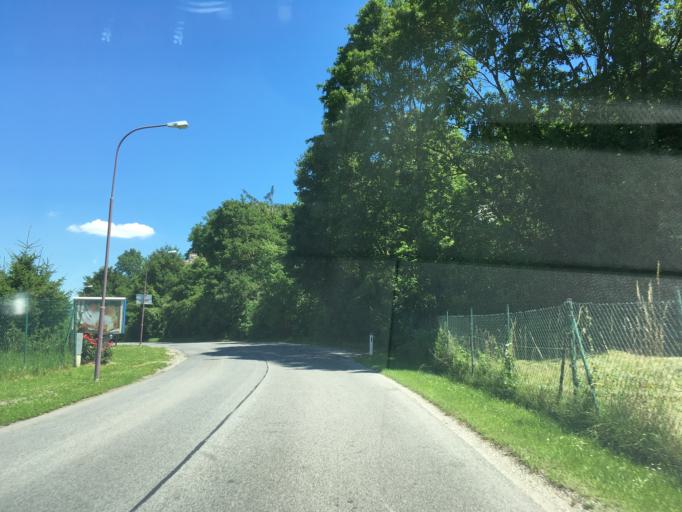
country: AT
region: Lower Austria
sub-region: Politischer Bezirk Neunkirchen
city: Pitten
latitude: 47.7192
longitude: 16.1956
